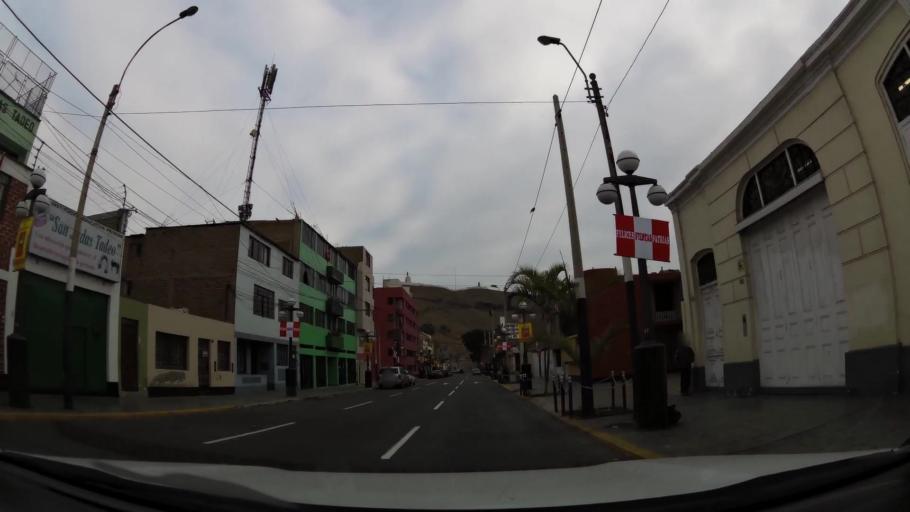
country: PE
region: Lima
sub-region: Lima
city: Surco
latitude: -12.1687
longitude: -77.0274
